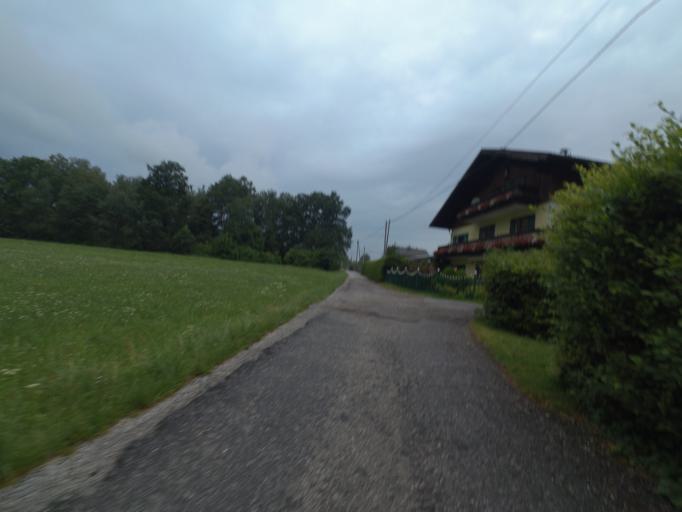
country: AT
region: Salzburg
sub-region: Politischer Bezirk Salzburg-Umgebung
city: Grodig
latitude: 47.7585
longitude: 13.0311
